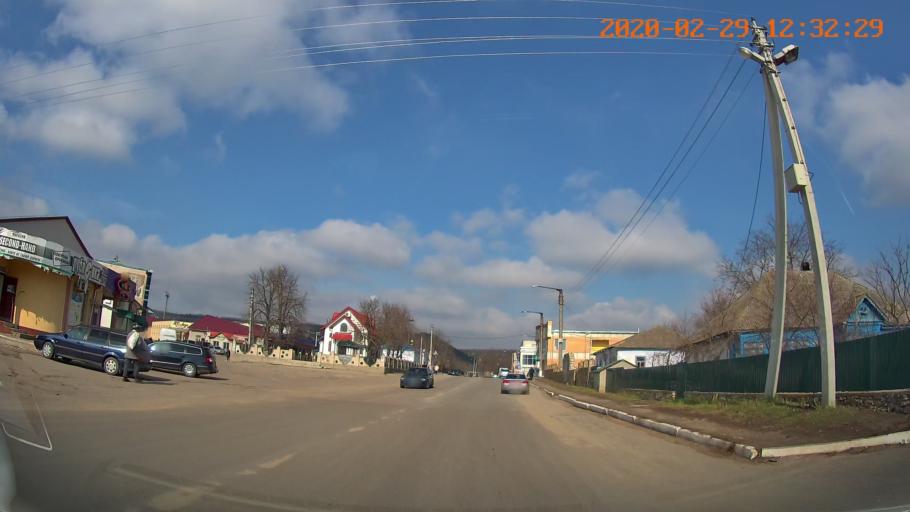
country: MD
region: Telenesti
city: Camenca
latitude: 48.0288
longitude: 28.7031
